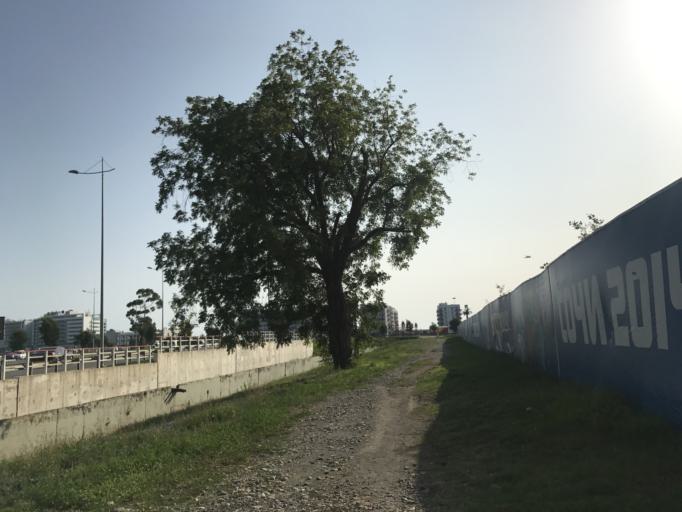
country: RU
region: Krasnodarskiy
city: Adler
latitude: 43.4156
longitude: 39.9387
